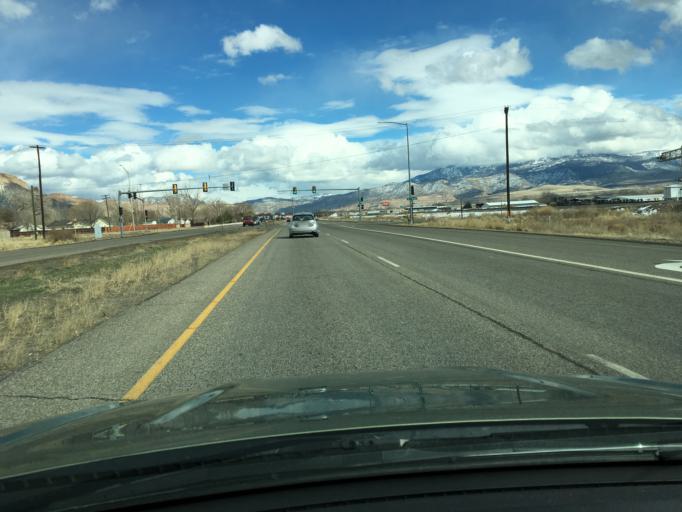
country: US
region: Colorado
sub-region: Mesa County
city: Clifton
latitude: 39.0837
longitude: -108.4697
